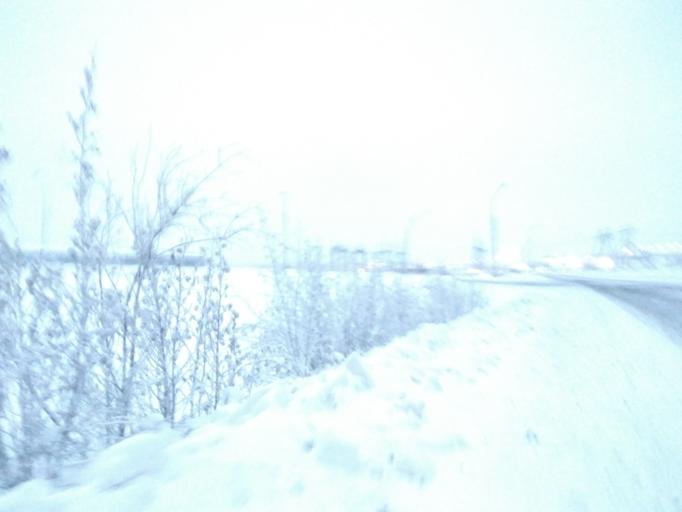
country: RU
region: Sakha
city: Aykhal
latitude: 65.9366
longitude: 111.5039
